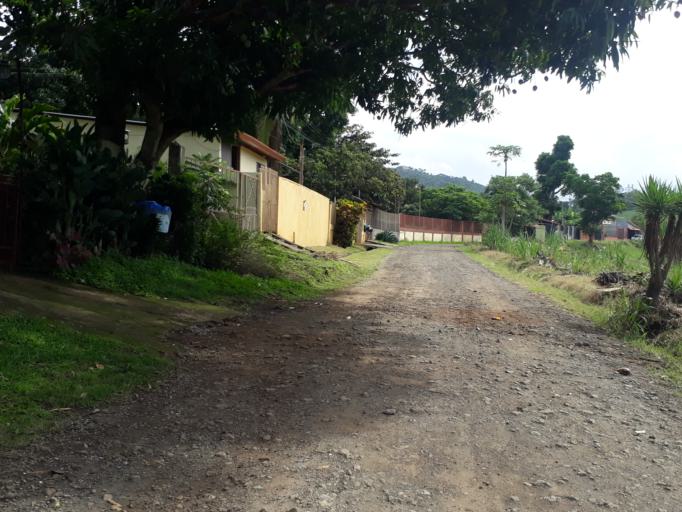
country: CR
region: Alajuela
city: Carrillos
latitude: 10.0259
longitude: -84.3377
